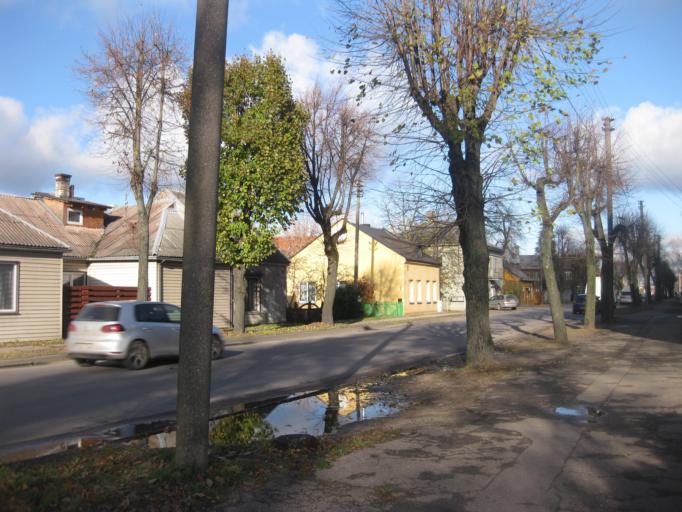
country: LT
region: Kauno apskritis
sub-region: Kaunas
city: Kaunas
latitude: 54.9122
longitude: 23.8906
